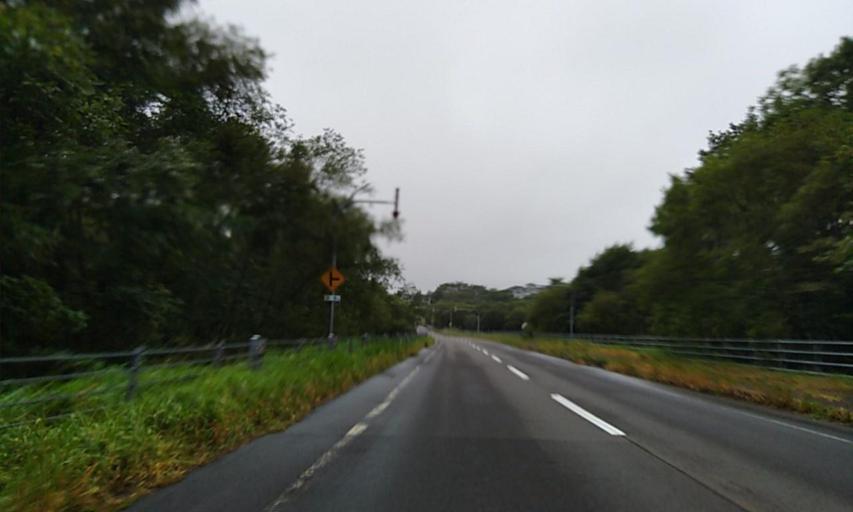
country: JP
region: Hokkaido
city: Shibetsu
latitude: 43.4898
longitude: 144.6390
